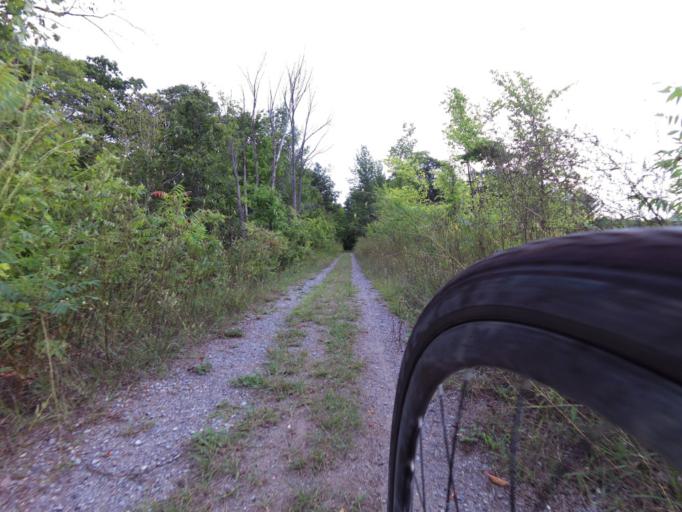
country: CA
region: Ontario
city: Perth
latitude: 44.6165
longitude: -76.2595
